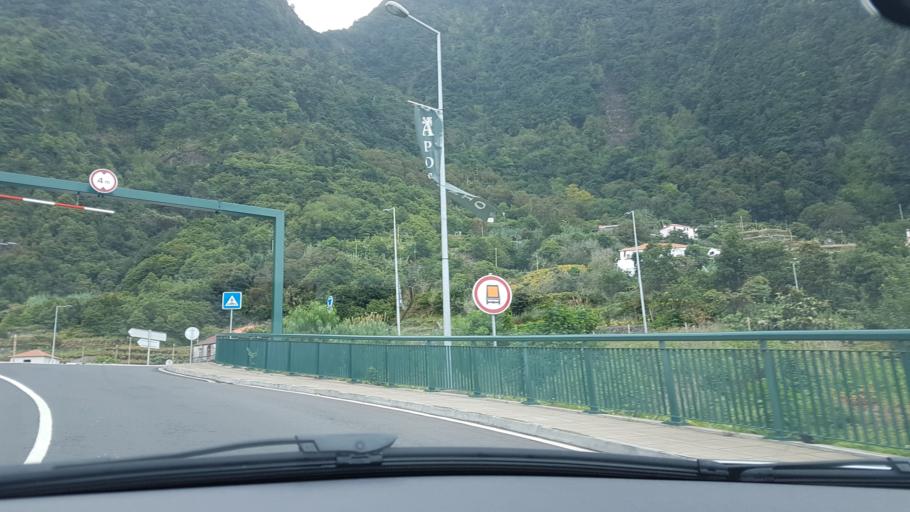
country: PT
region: Madeira
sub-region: Sao Vicente
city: Sao Vicente
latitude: 32.8221
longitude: -16.9907
